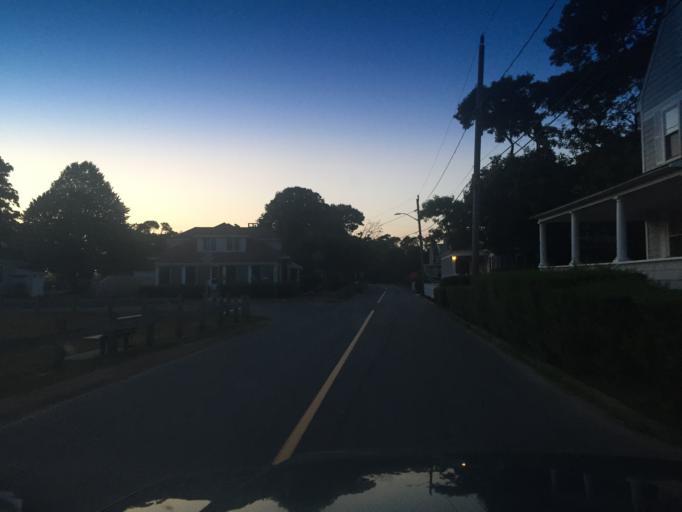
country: US
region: Massachusetts
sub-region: Barnstable County
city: Falmouth
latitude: 41.5461
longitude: -70.5972
